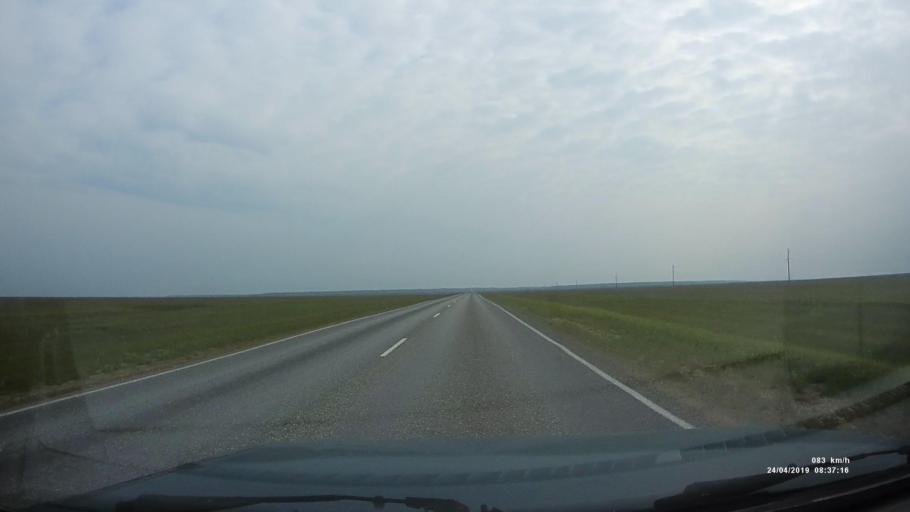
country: RU
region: Kalmykiya
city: Arshan'
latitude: 46.2091
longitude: 43.9482
